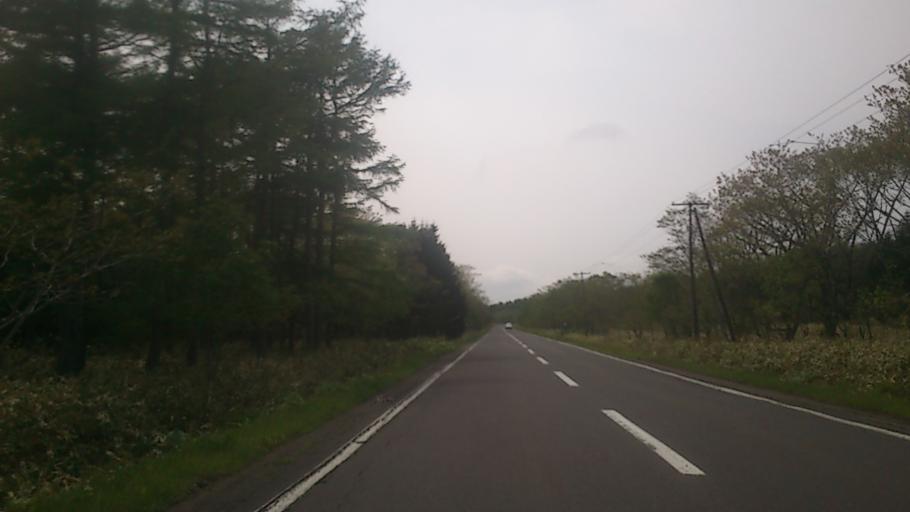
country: JP
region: Hokkaido
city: Nemuro
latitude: 43.2073
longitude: 145.3430
